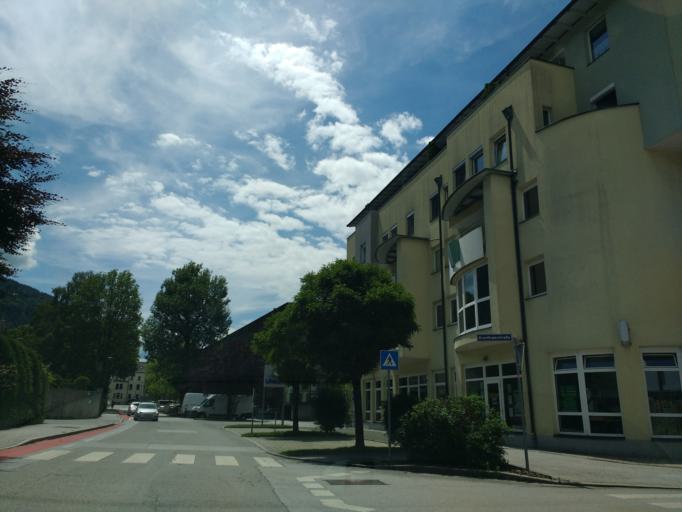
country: AT
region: Tyrol
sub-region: Politischer Bezirk Kufstein
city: Kufstein
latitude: 47.5846
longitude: 12.1743
